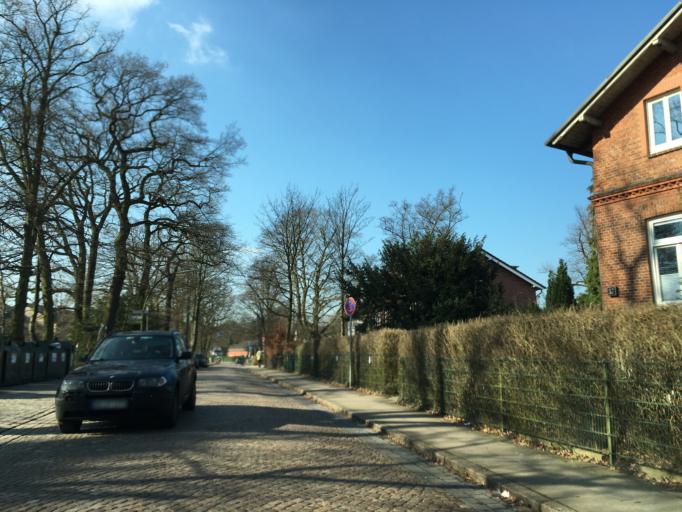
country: DE
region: Hamburg
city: Eidelstedt
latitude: 53.5574
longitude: 9.8619
